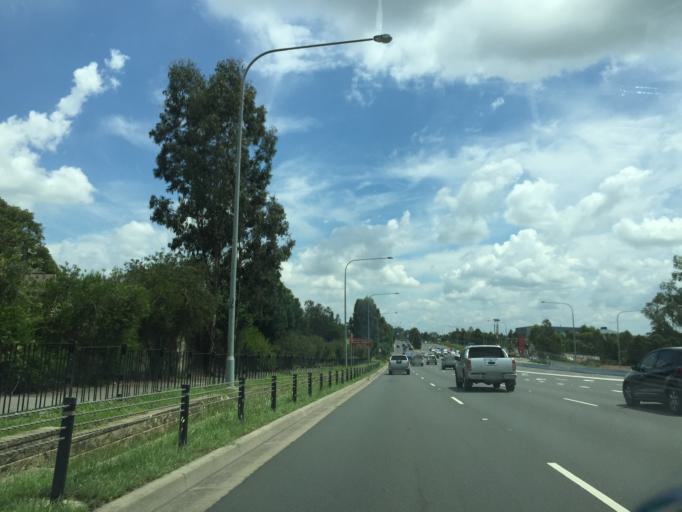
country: AU
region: New South Wales
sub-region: The Hills Shire
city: Beaumont Hills
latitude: -33.6957
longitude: 150.9265
